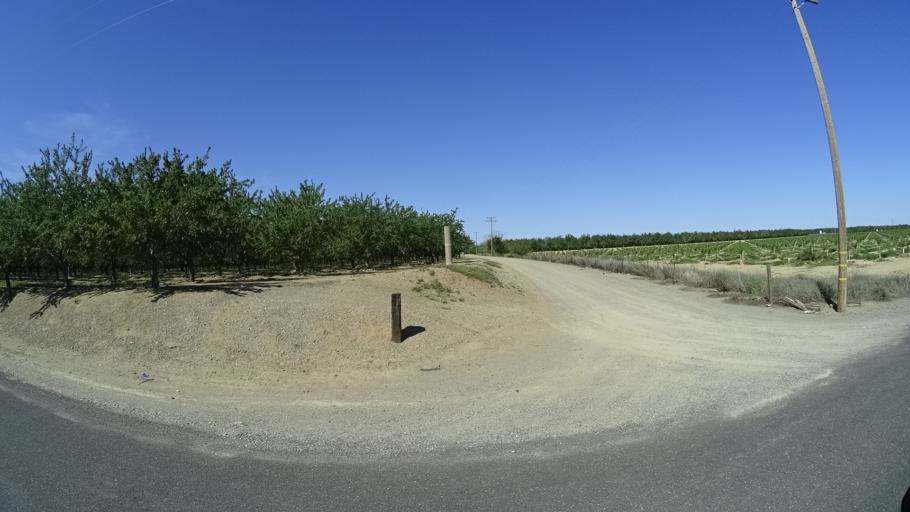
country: US
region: California
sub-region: Glenn County
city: Hamilton City
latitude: 39.6666
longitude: -122.1033
